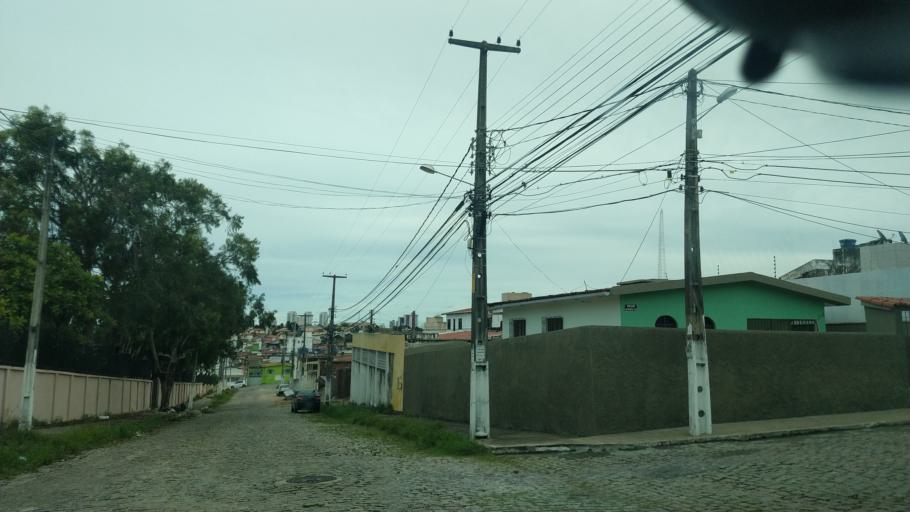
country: BR
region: Rio Grande do Norte
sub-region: Natal
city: Natal
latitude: -5.8413
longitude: -35.2072
